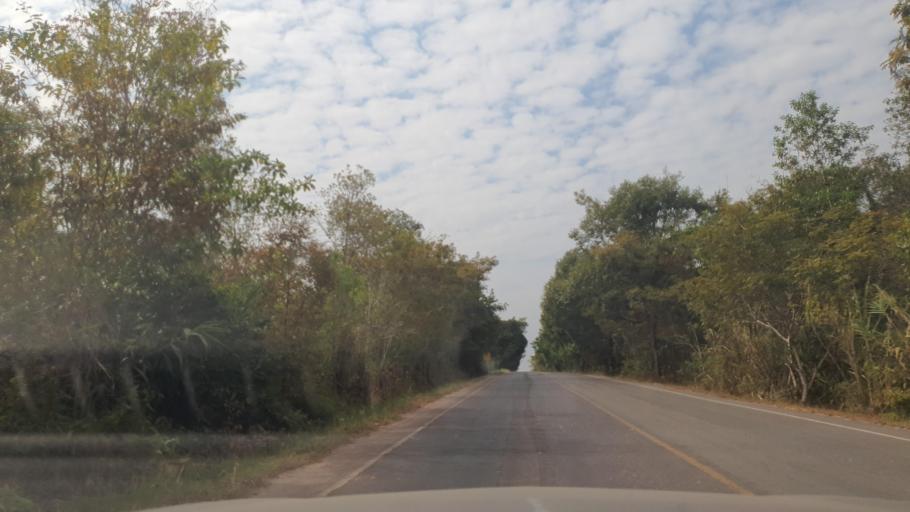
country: TH
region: Changwat Bueng Kan
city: Bung Khla
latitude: 18.2949
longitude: 103.9276
